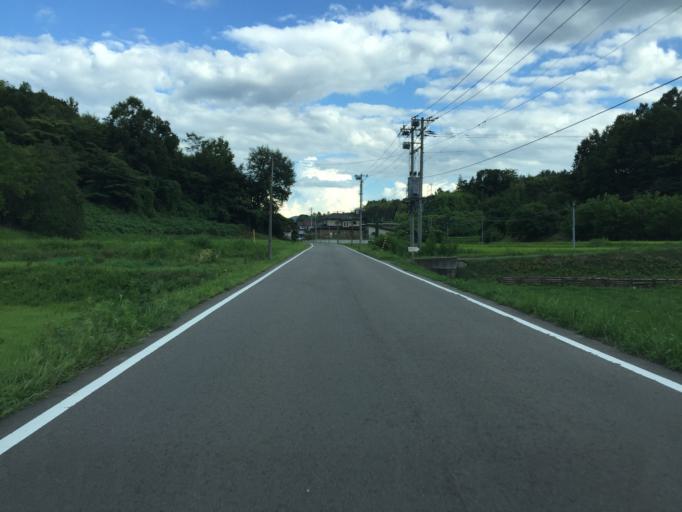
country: JP
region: Fukushima
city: Fukushima-shi
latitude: 37.6818
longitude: 140.5724
